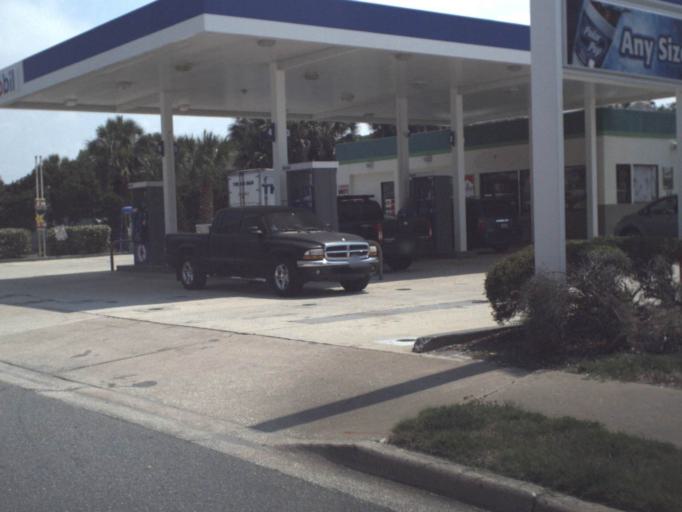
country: US
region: Florida
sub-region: Duval County
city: Neptune Beach
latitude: 30.3039
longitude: -81.3950
